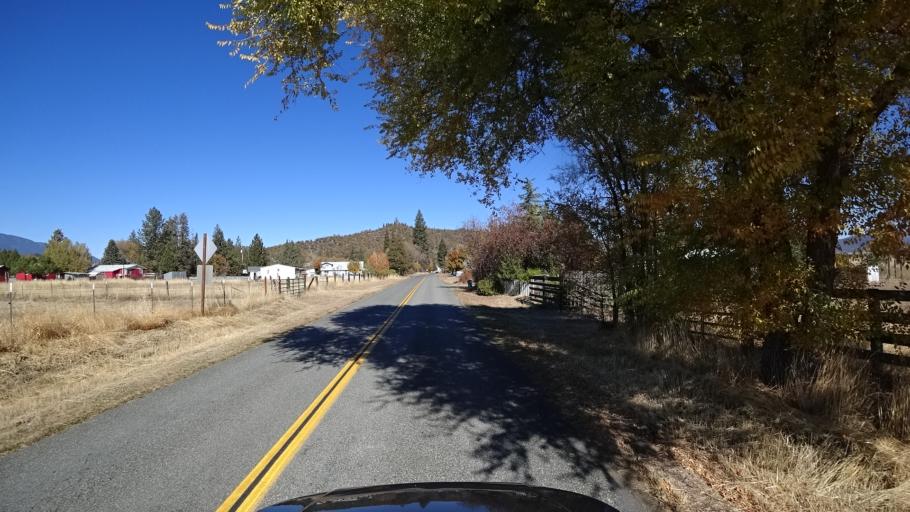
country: US
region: California
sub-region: Siskiyou County
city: Yreka
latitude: 41.5457
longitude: -122.9067
